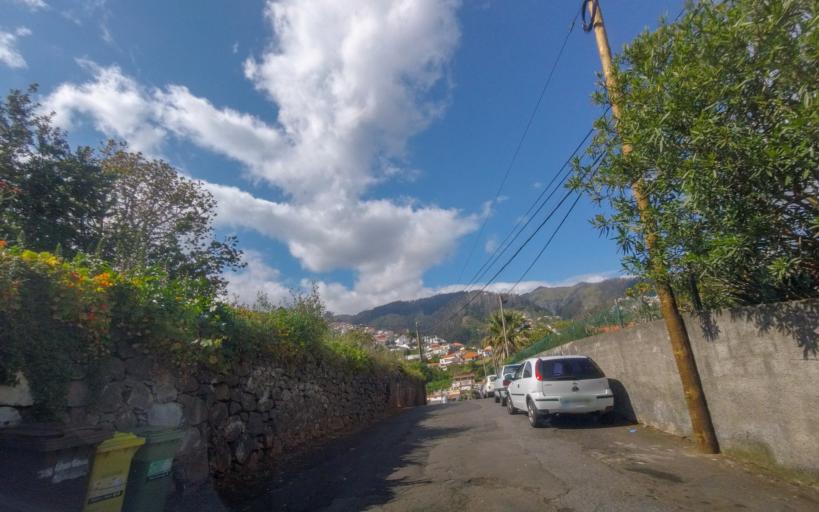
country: PT
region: Madeira
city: Camara de Lobos
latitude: 32.6727
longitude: -16.9471
